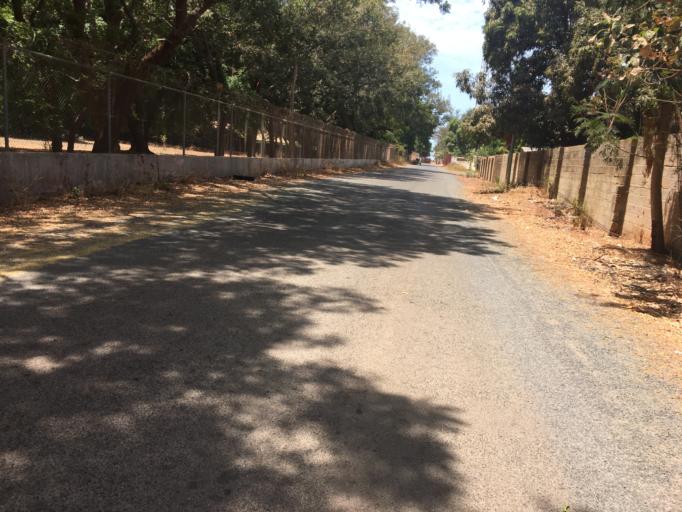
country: GM
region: Banjul
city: Bakau
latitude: 13.4749
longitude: -16.6856
